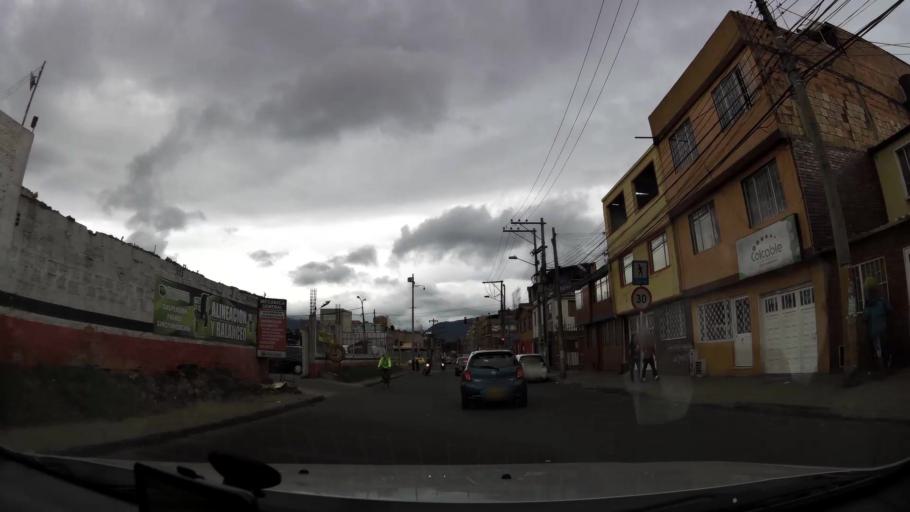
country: CO
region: Bogota D.C.
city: Bogota
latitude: 4.5986
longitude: -74.1365
